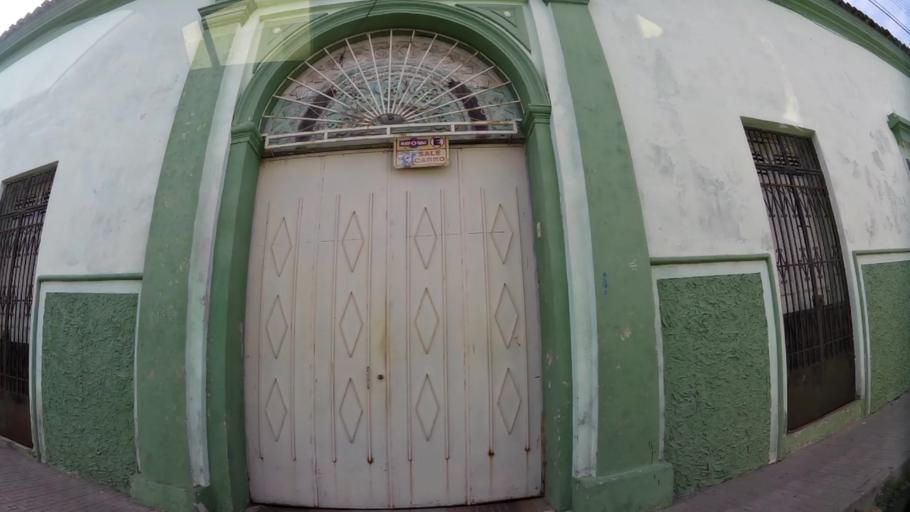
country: SV
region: Santa Ana
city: Chalchuapa
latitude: 13.9830
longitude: -89.6792
